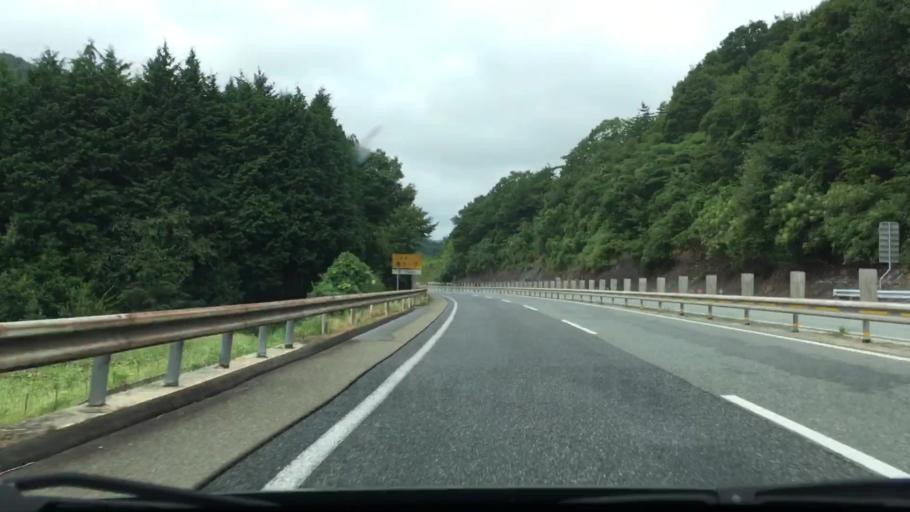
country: JP
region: Hiroshima
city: Shobara
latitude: 34.8526
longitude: 133.0943
